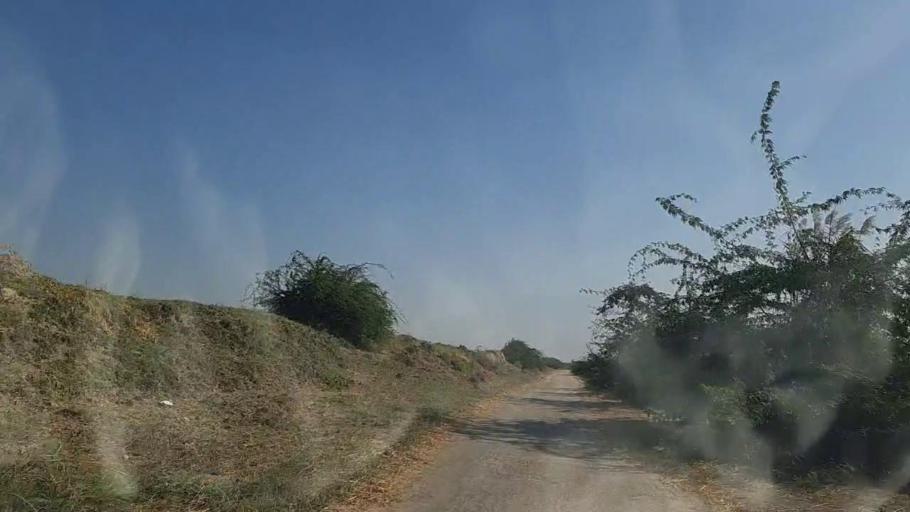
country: PK
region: Sindh
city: Mirpur Batoro
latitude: 24.6059
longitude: 68.1724
